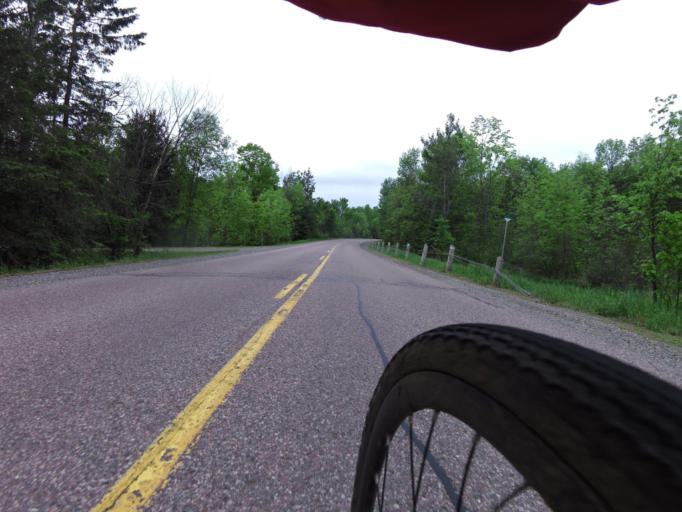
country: CA
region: Ontario
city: Renfrew
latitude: 45.2909
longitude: -76.6953
